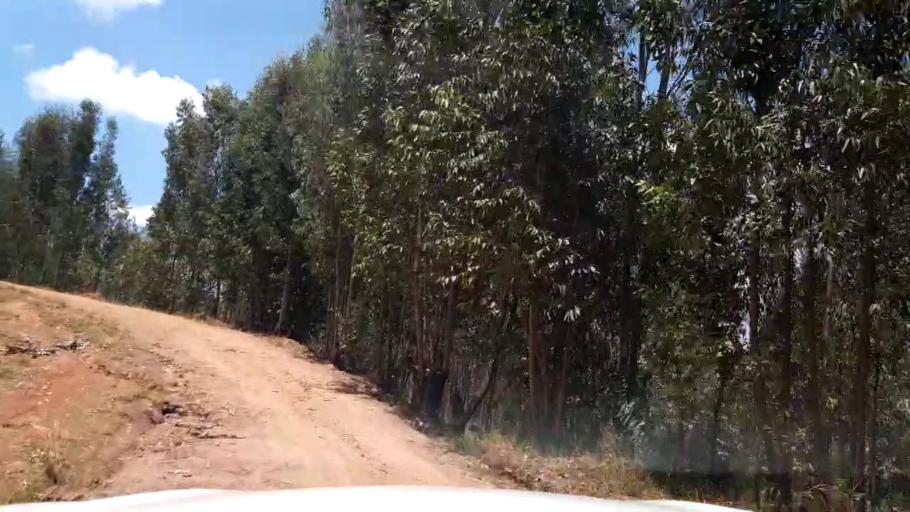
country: RW
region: Northern Province
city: Byumba
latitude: -1.5258
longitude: 30.1760
